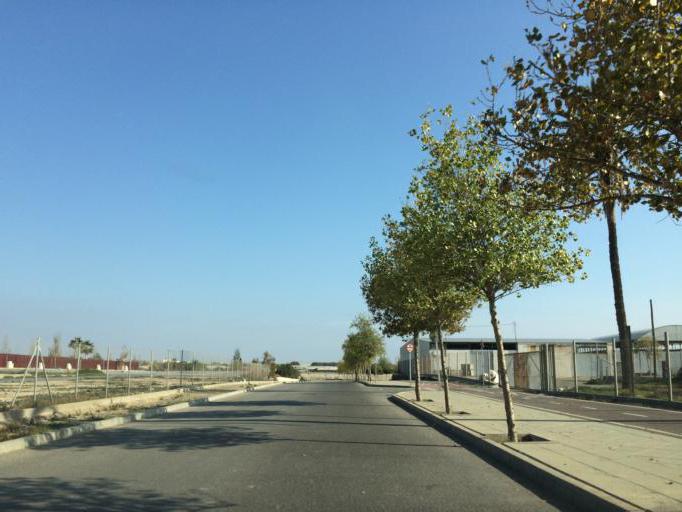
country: ES
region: Andalusia
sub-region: Provincia de Almeria
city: Almeria
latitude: 36.8322
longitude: -2.4308
